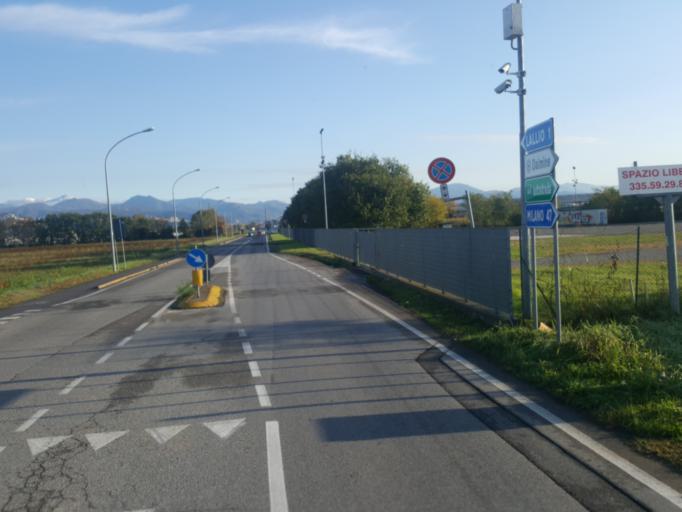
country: IT
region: Lombardy
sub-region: Provincia di Bergamo
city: Lallio
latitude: 45.6574
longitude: 9.6161
